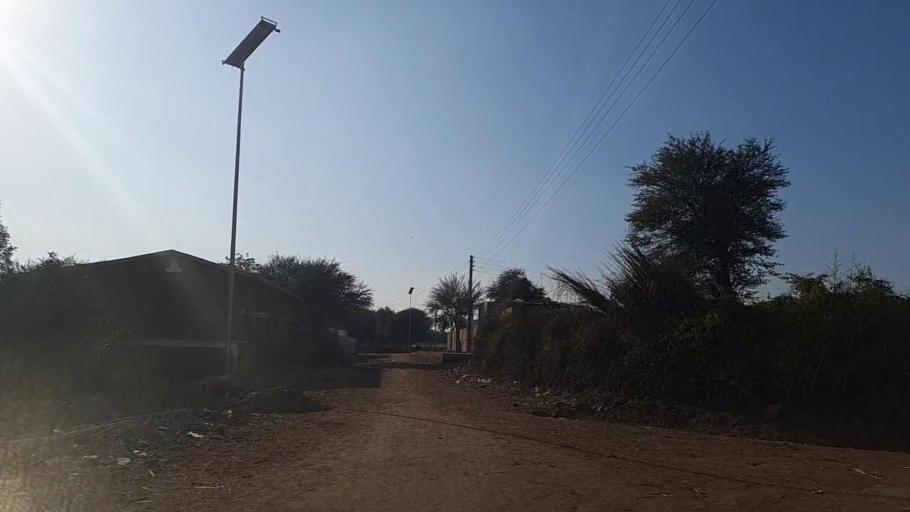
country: PK
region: Sindh
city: Shahpur Chakar
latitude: 26.1974
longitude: 68.6332
